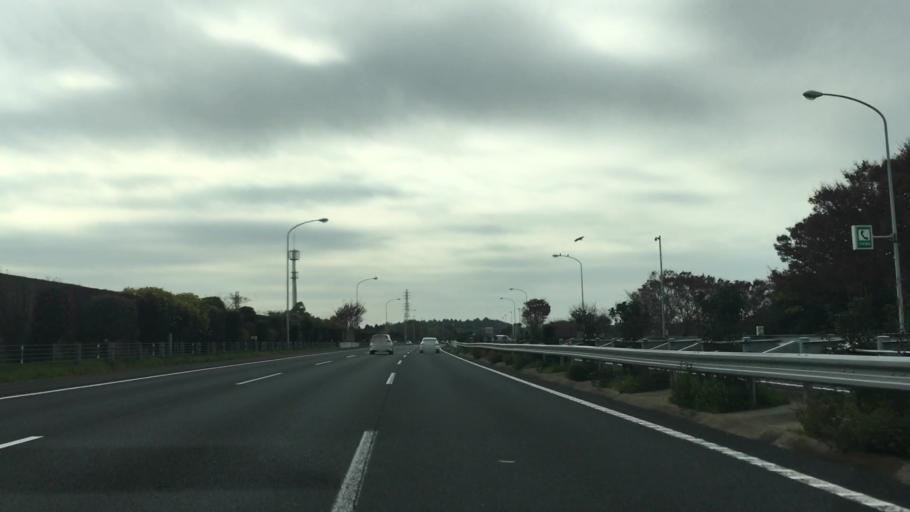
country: JP
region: Chiba
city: Narita
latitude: 35.7446
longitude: 140.3121
